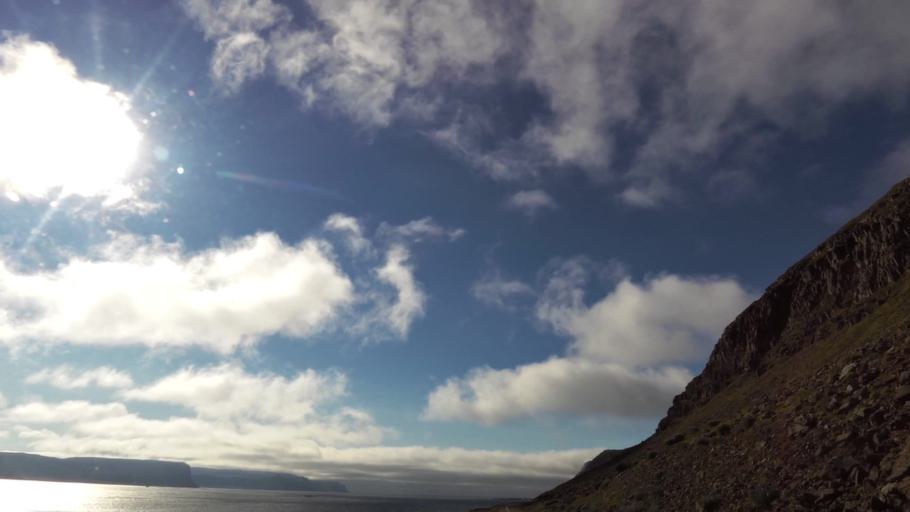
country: IS
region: West
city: Olafsvik
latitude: 65.5699
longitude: -23.9310
